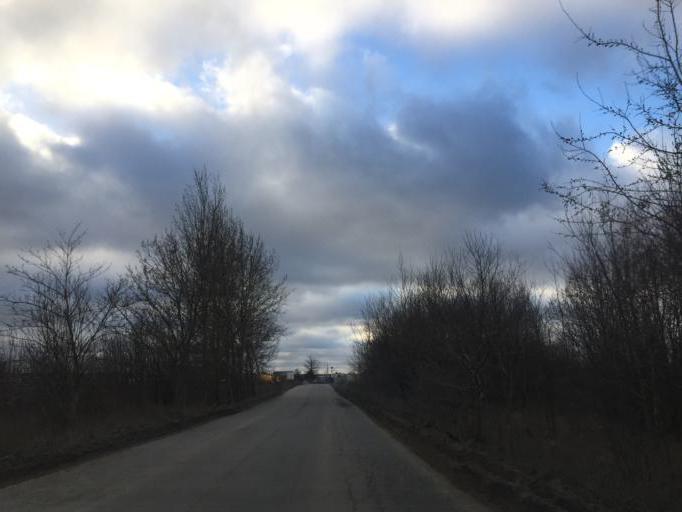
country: PL
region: Pomeranian Voivodeship
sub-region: Gdynia
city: Wielki Kack
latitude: 54.4147
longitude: 18.4699
